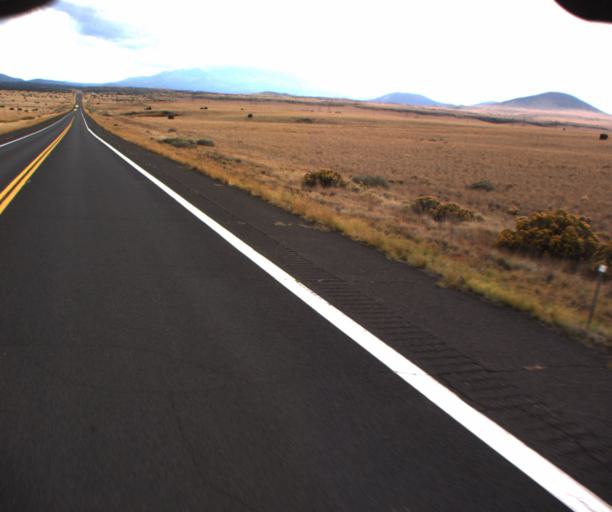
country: US
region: Arizona
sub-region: Coconino County
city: Flagstaff
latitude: 35.5663
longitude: -111.5329
